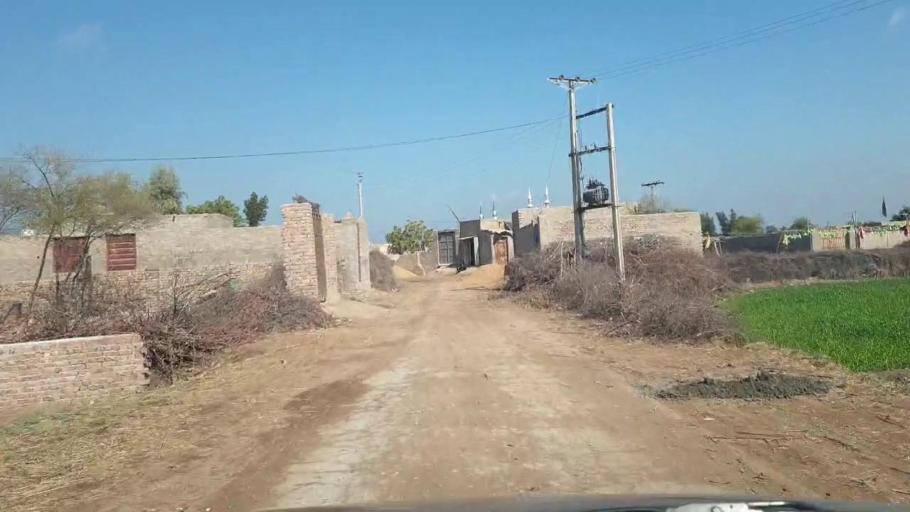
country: PK
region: Sindh
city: Bhit Shah
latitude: 25.8943
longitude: 68.5271
